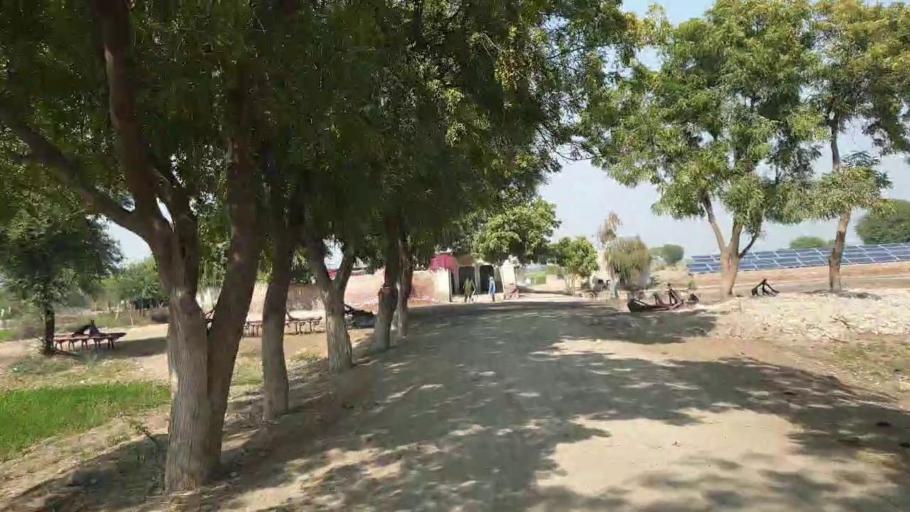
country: PK
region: Sindh
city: Mirwah Gorchani
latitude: 25.3715
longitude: 68.9297
